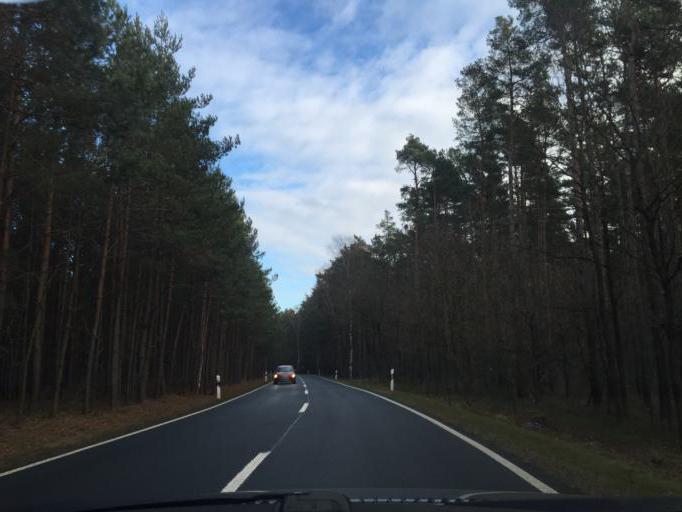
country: DE
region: Saxony
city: Radeburg
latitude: 51.2426
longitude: 13.7592
